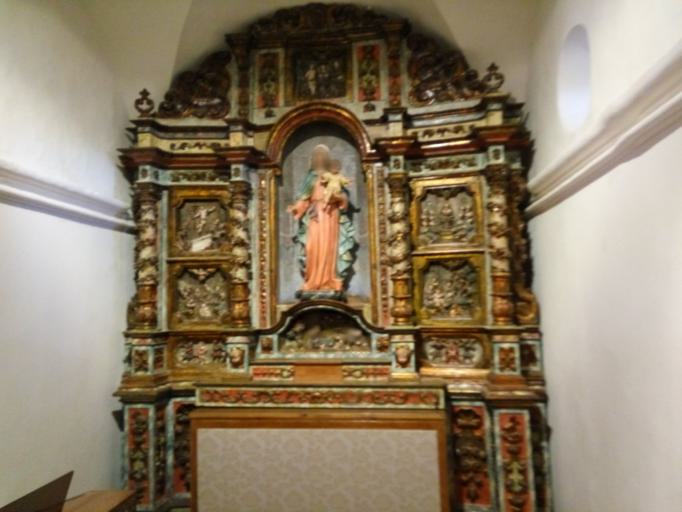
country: ES
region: Catalonia
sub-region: Provincia de Barcelona
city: Capolat
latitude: 42.0332
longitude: 1.7432
